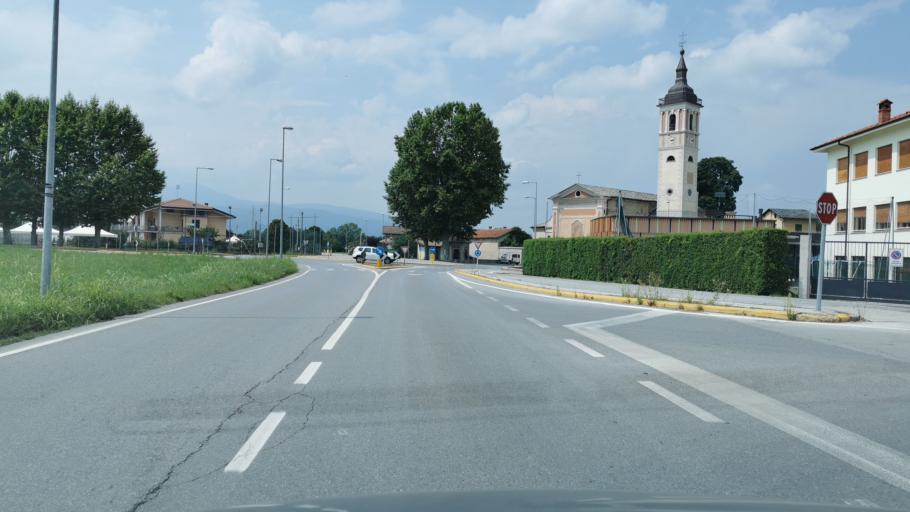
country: IT
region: Piedmont
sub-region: Provincia di Cuneo
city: Roata Rossi
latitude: 44.4320
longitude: 7.5056
